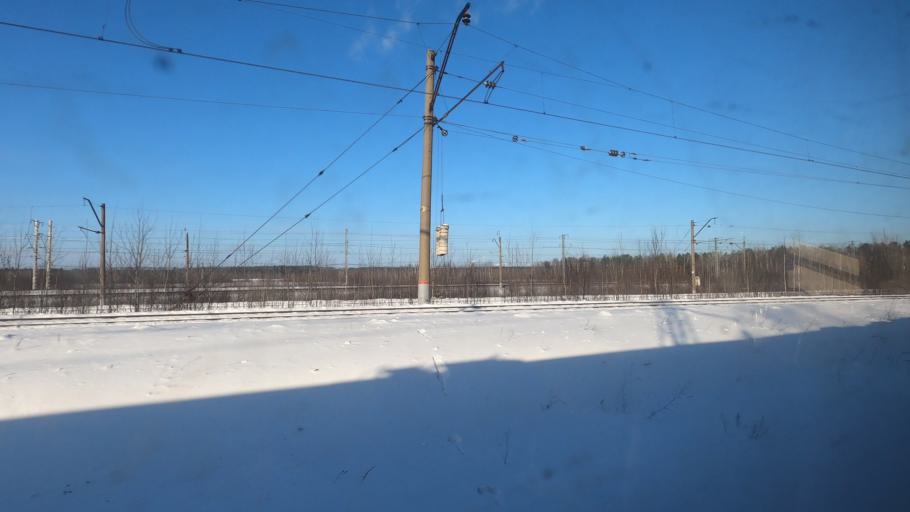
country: RU
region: Moskovskaya
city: Fryazevo
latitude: 55.7257
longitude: 38.4368
